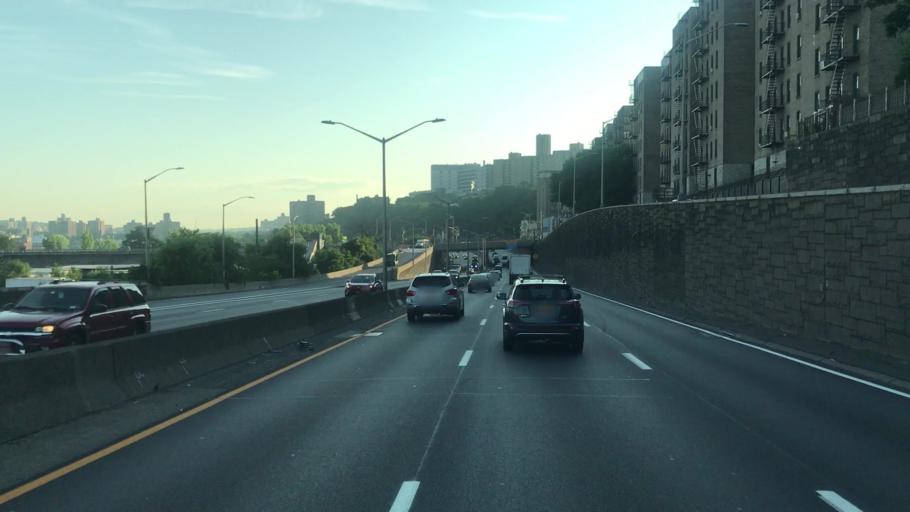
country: US
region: New York
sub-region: New York County
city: Inwood
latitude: 40.8601
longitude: -73.9149
